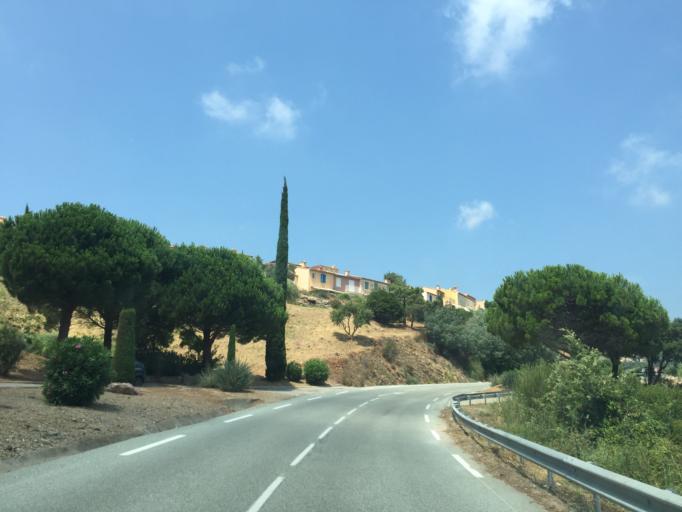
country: FR
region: Provence-Alpes-Cote d'Azur
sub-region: Departement du Var
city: Sainte-Maxime
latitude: 43.3532
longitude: 6.6744
